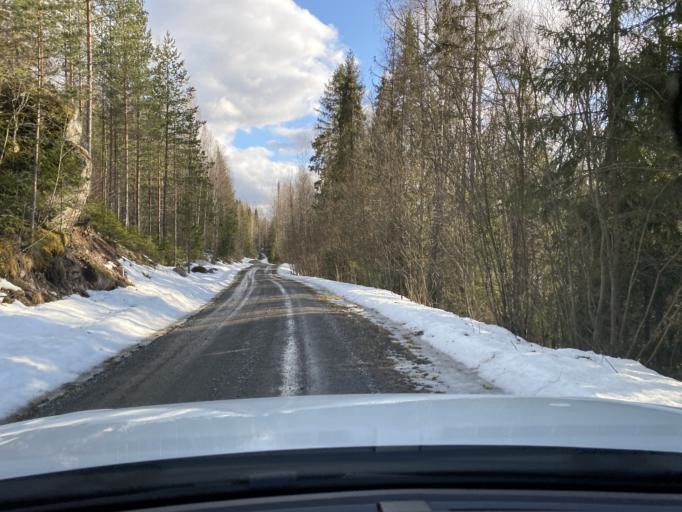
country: FI
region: Pirkanmaa
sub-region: Lounais-Pirkanmaa
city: Mouhijaervi
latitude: 61.4513
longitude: 22.9590
